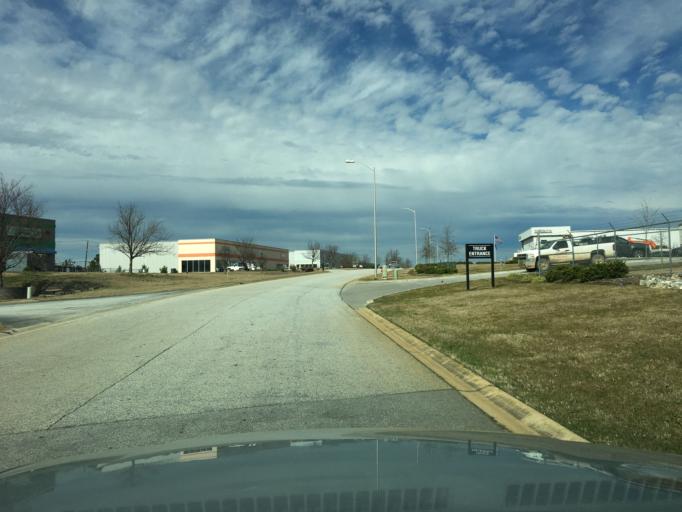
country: US
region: South Carolina
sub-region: Spartanburg County
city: Duncan
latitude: 34.9052
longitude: -82.1857
